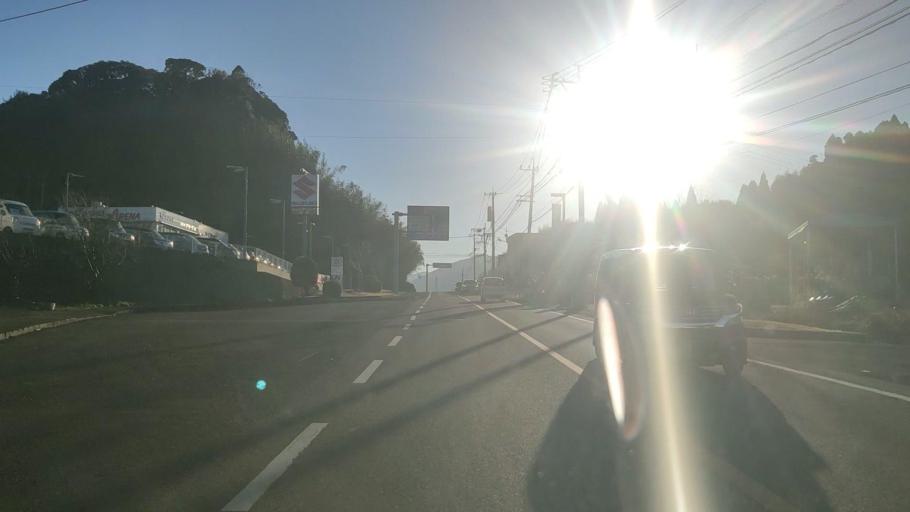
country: JP
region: Miyazaki
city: Miyazaki-shi
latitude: 31.8656
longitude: 131.3895
